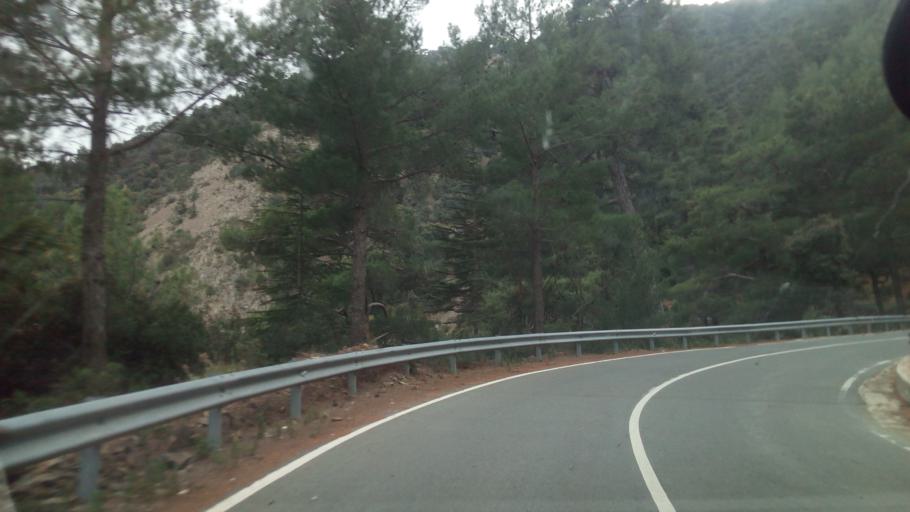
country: CY
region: Lefkosia
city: Kato Pyrgos
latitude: 34.9996
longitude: 32.6937
